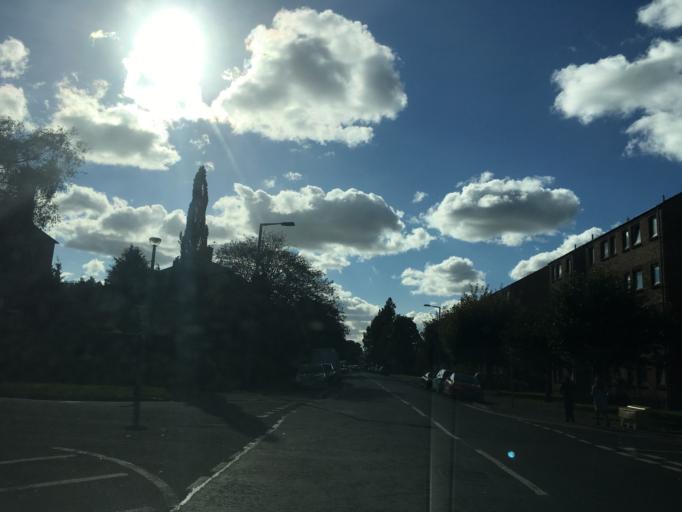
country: GB
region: Scotland
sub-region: Edinburgh
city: Colinton
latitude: 55.9317
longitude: -3.2421
